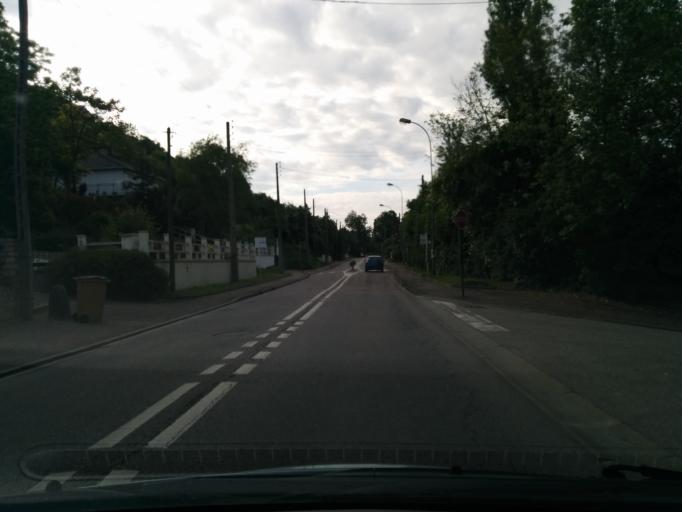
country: FR
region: Ile-de-France
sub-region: Departement des Yvelines
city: Follainville-Dennemont
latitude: 49.0084
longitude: 1.7111
